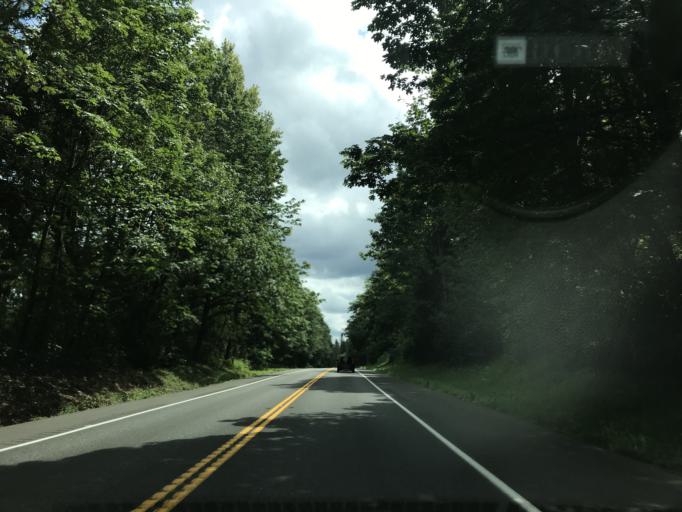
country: US
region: Washington
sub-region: King County
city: Maple Valley
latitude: 47.4194
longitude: -122.0708
